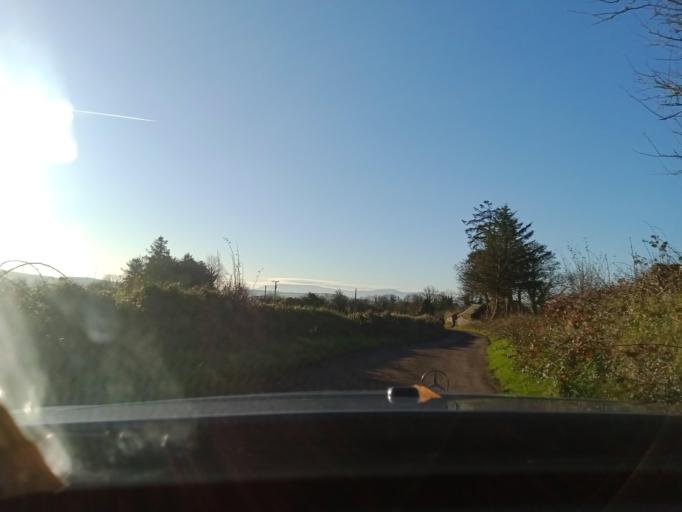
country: IE
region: Leinster
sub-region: Kilkenny
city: Callan
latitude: 52.4577
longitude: -7.4236
